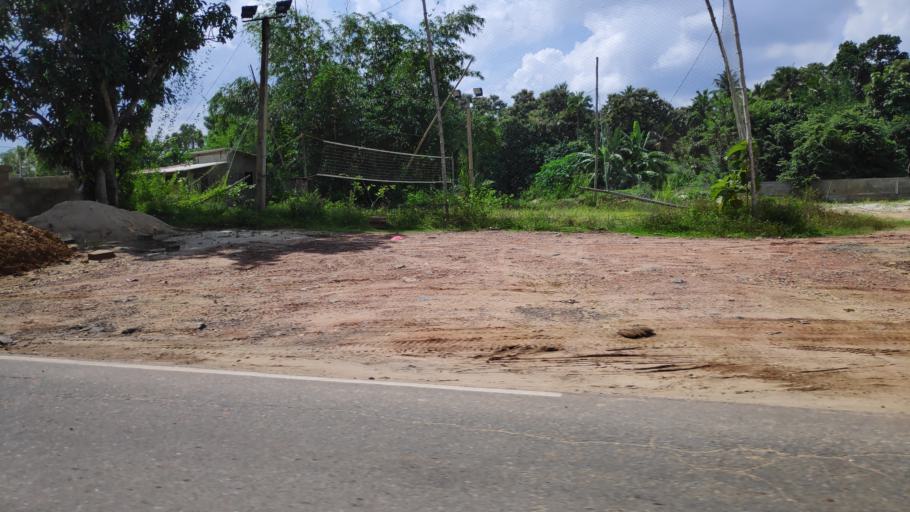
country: LK
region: Western
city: Minuwangoda
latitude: 7.2816
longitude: 80.0543
